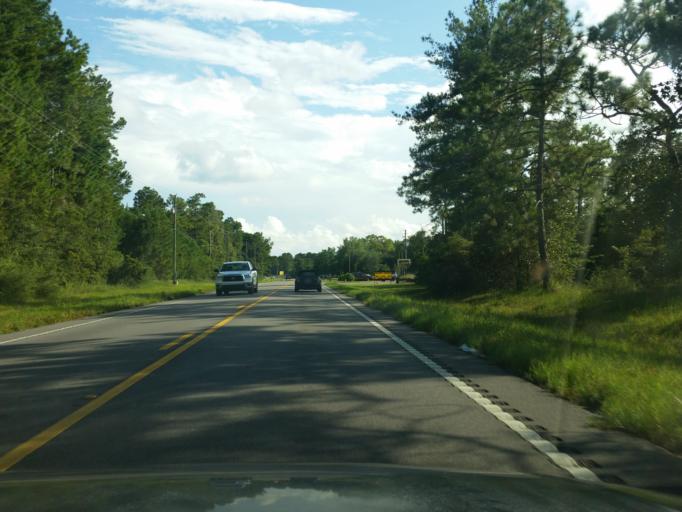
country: US
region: Alabama
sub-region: Mobile County
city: Theodore
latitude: 30.4513
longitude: -88.1161
